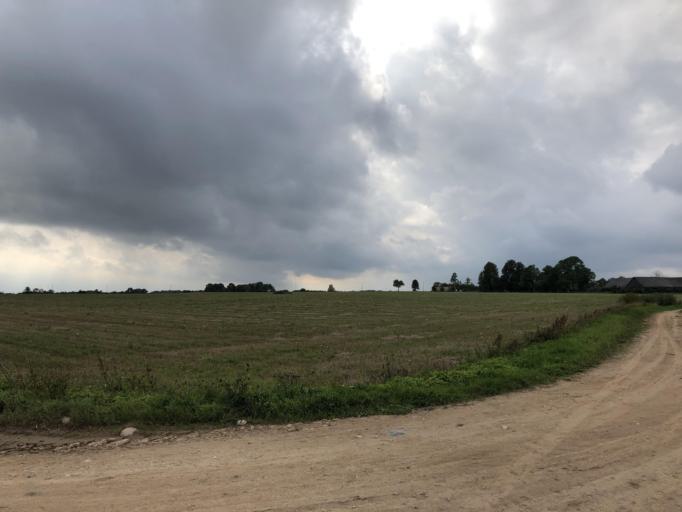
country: LV
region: Talsu Rajons
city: Sabile
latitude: 56.9727
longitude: 22.4020
